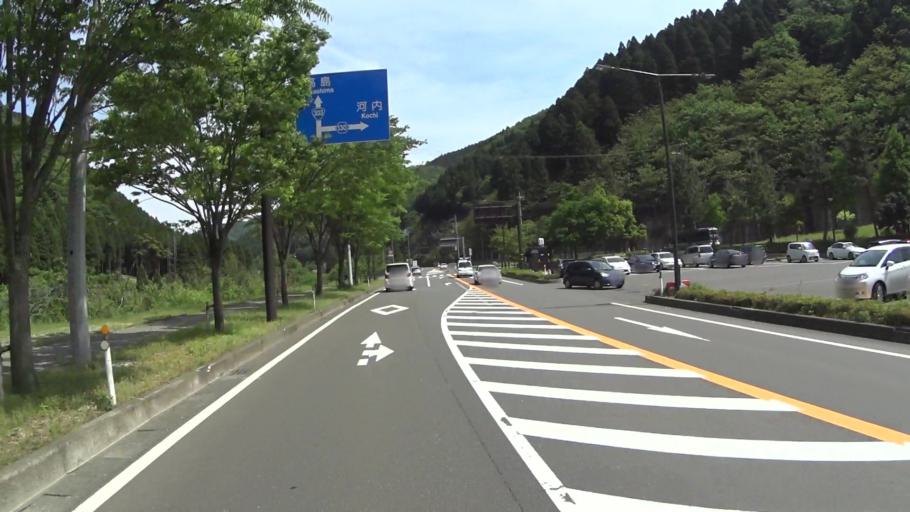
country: JP
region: Fukui
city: Obama
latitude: 35.4411
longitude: 135.9064
